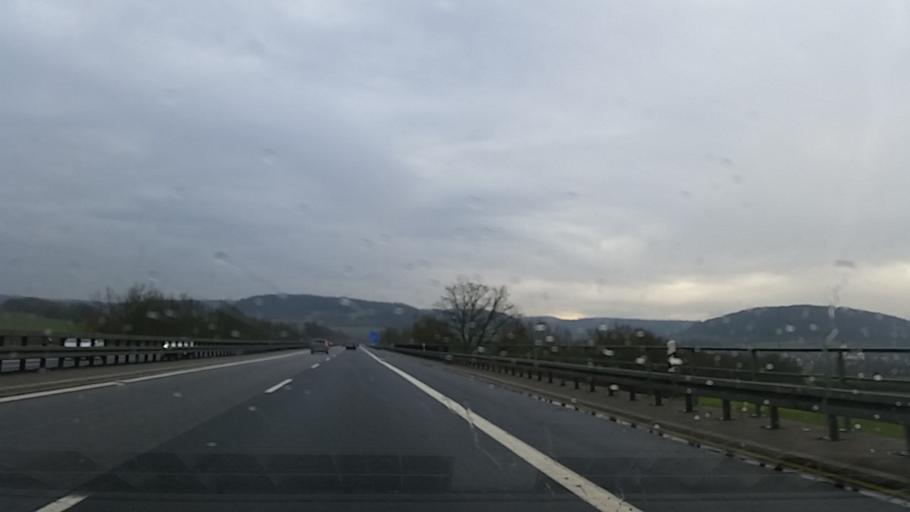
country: DE
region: Bavaria
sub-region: Regierungsbezirk Unterfranken
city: Elfershausen
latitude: 50.1355
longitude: 9.9526
